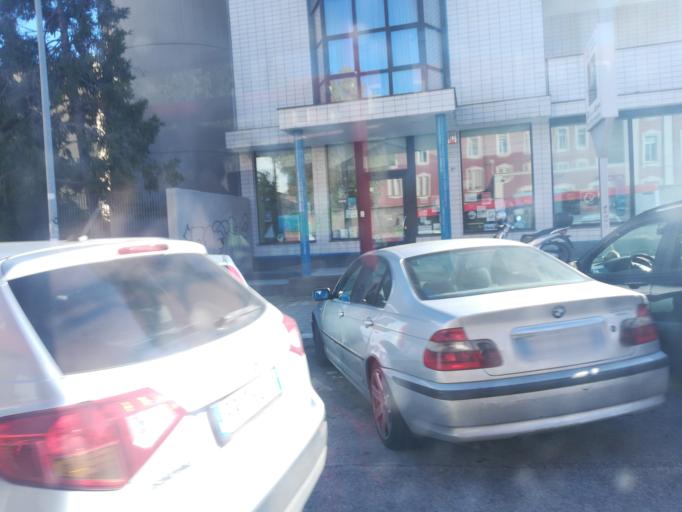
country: IT
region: Apulia
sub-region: Provincia di Bari
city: Bari
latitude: 41.1131
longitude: 16.8790
